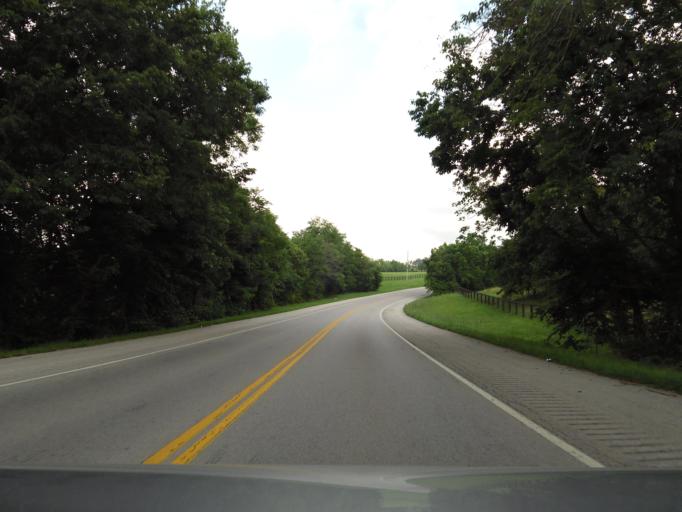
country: US
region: Kentucky
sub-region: Bourbon County
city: Paris
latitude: 38.2340
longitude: -84.2770
